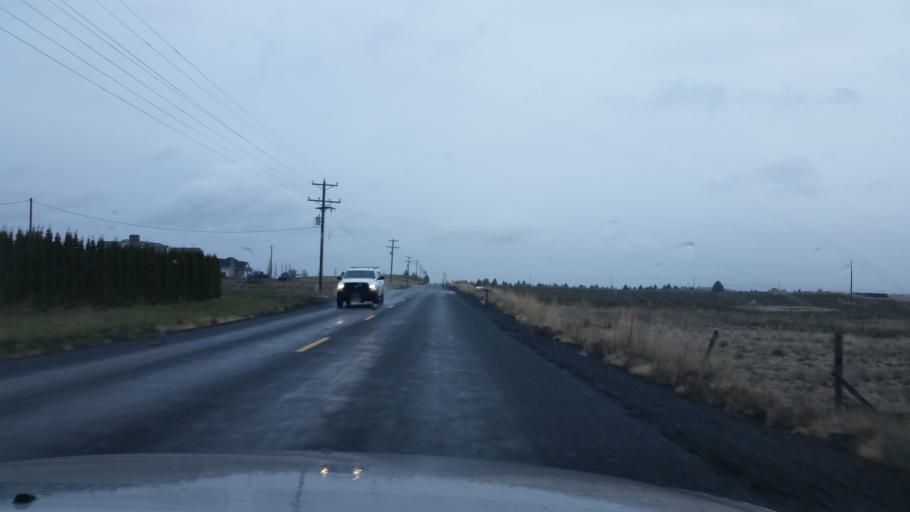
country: US
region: Washington
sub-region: Spokane County
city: Airway Heights
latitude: 47.6655
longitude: -117.6038
